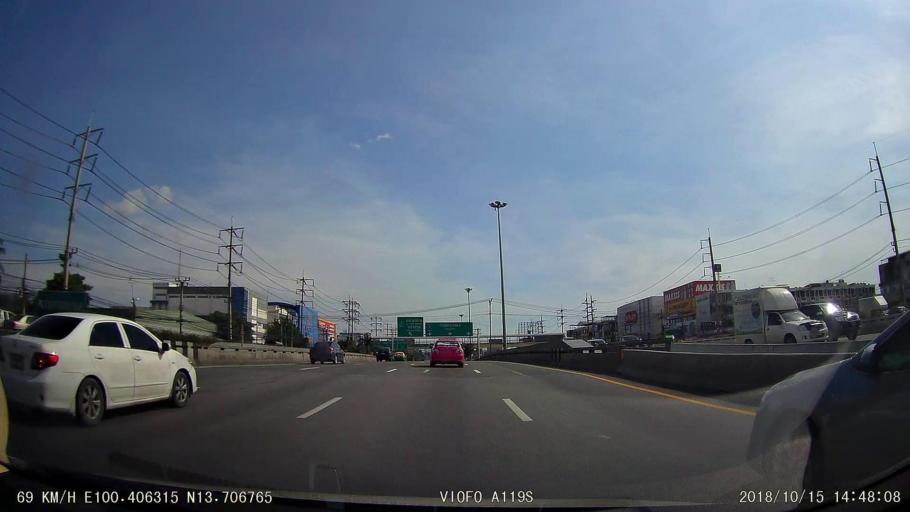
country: TH
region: Bangkok
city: Bang Khae
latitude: 13.7065
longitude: 100.4065
